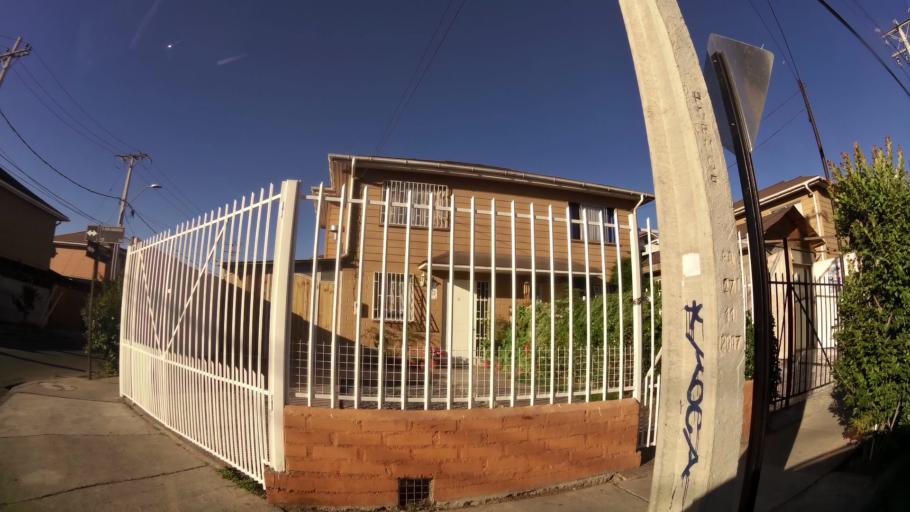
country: CL
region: Santiago Metropolitan
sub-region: Provincia de Maipo
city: San Bernardo
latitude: -33.6066
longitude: -70.6708
